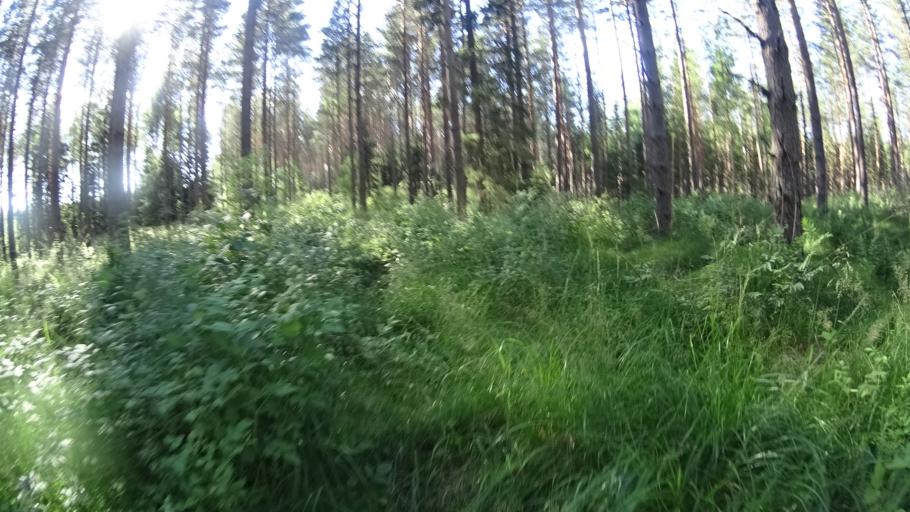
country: FI
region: Uusimaa
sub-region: Helsinki
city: Karkkila
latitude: 60.6499
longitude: 24.1593
